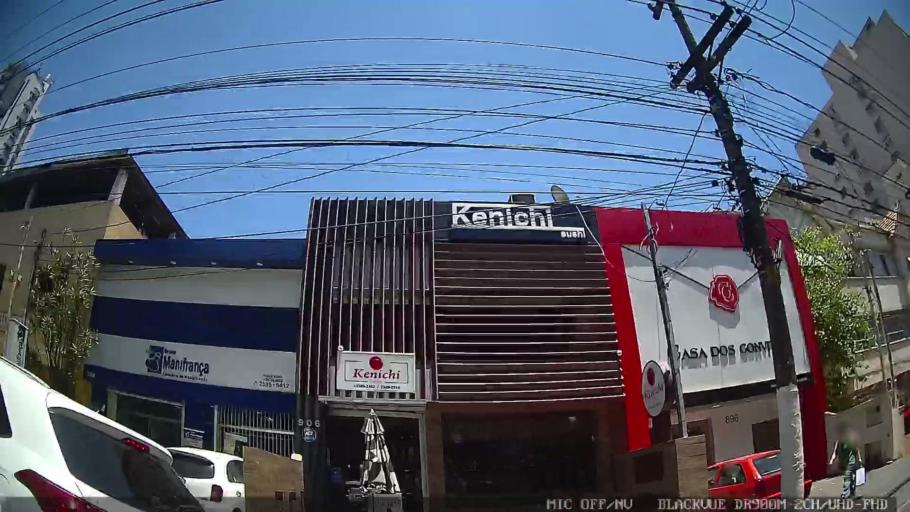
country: BR
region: Sao Paulo
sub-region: Sao Paulo
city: Sao Paulo
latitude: -23.5629
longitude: -46.5977
